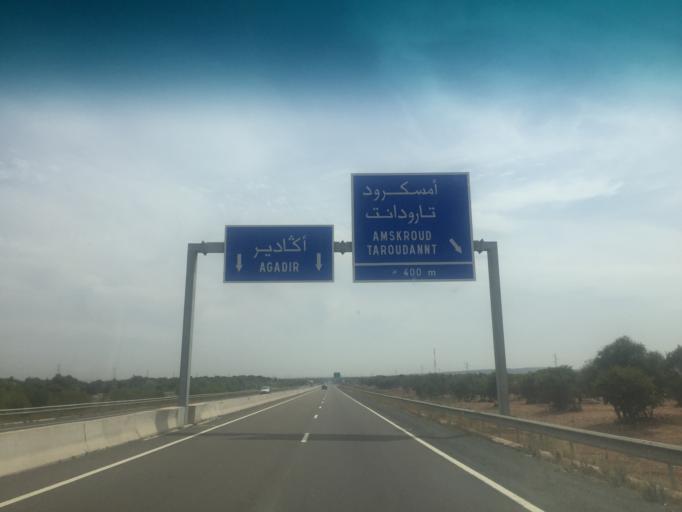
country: MA
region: Souss-Massa-Draa
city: Oulad Teima
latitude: 30.4921
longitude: -9.3399
